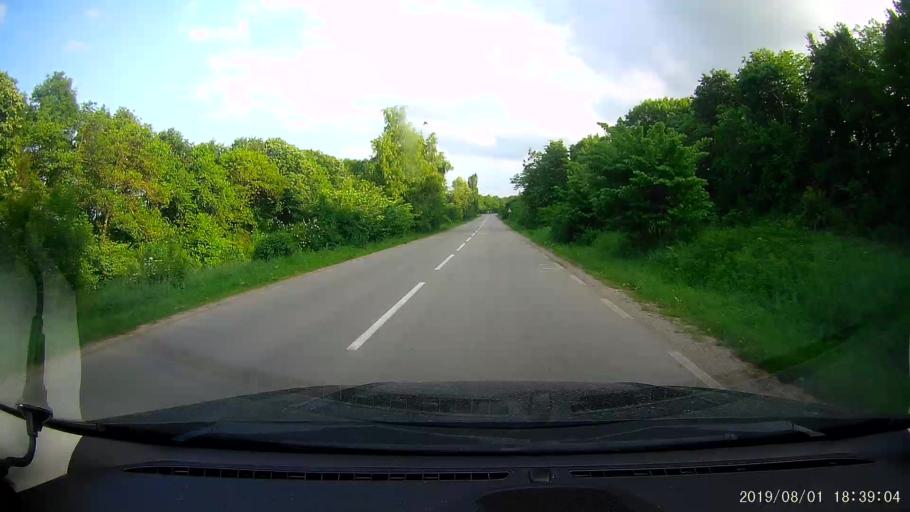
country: BG
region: Shumen
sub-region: Obshtina Khitrino
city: Gara Khitrino
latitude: 43.3933
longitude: 26.9173
